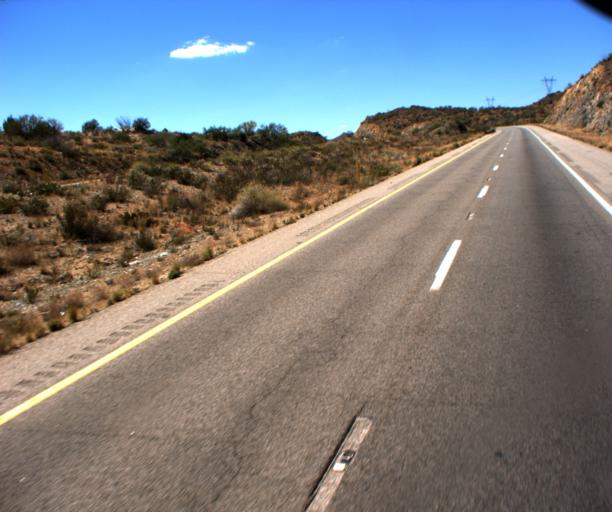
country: US
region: Arizona
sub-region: Yavapai County
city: Bagdad
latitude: 34.4539
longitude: -113.2886
